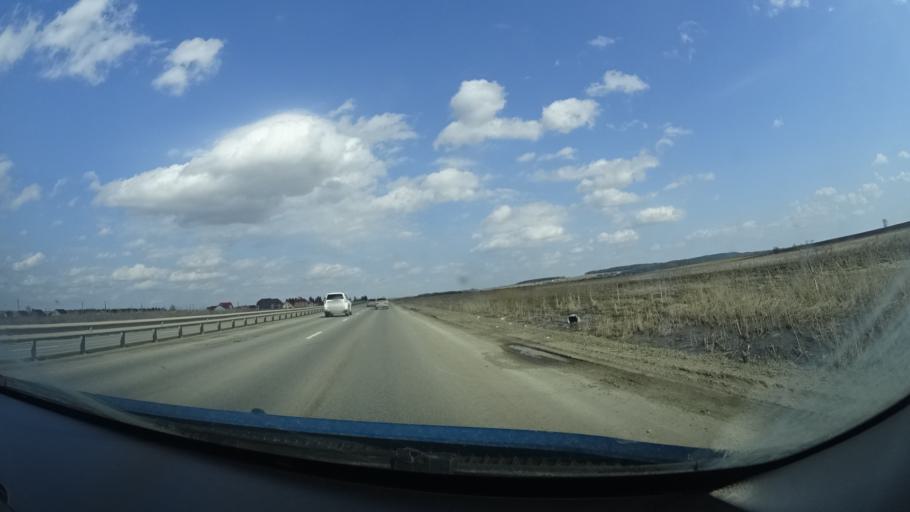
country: RU
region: Perm
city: Kultayevo
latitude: 57.8916
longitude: 55.9503
